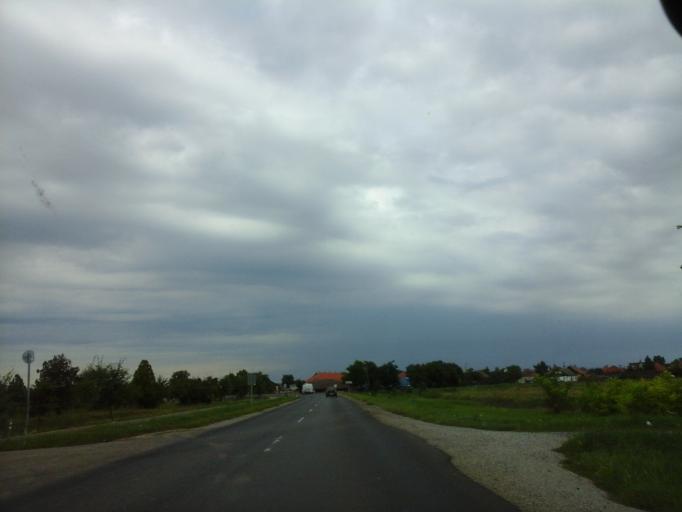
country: HU
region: Hajdu-Bihar
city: Balmazujvaros
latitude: 47.5980
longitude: 21.3384
